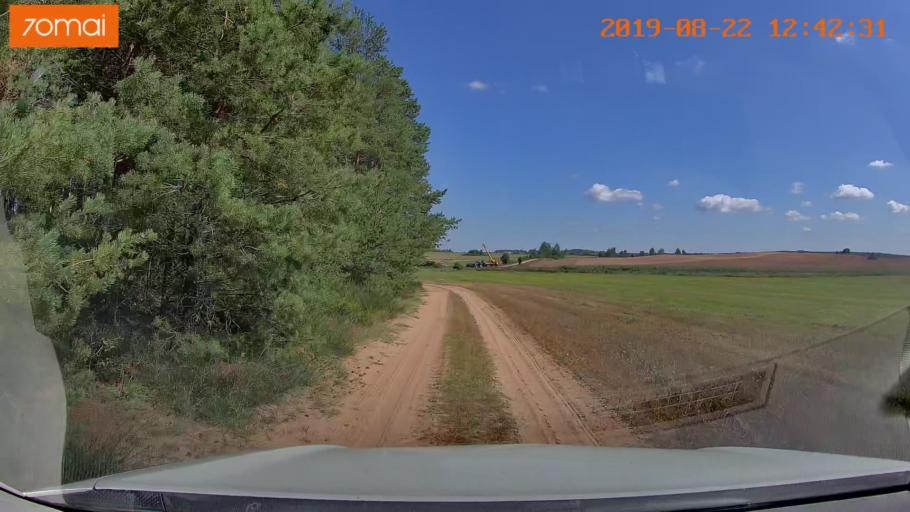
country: BY
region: Minsk
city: Prawdzinski
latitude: 53.4505
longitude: 27.5979
